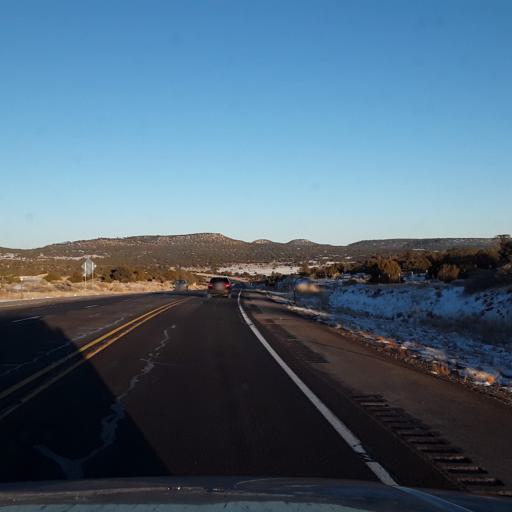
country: US
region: New Mexico
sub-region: Lincoln County
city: Carrizozo
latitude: 34.2377
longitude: -105.6084
